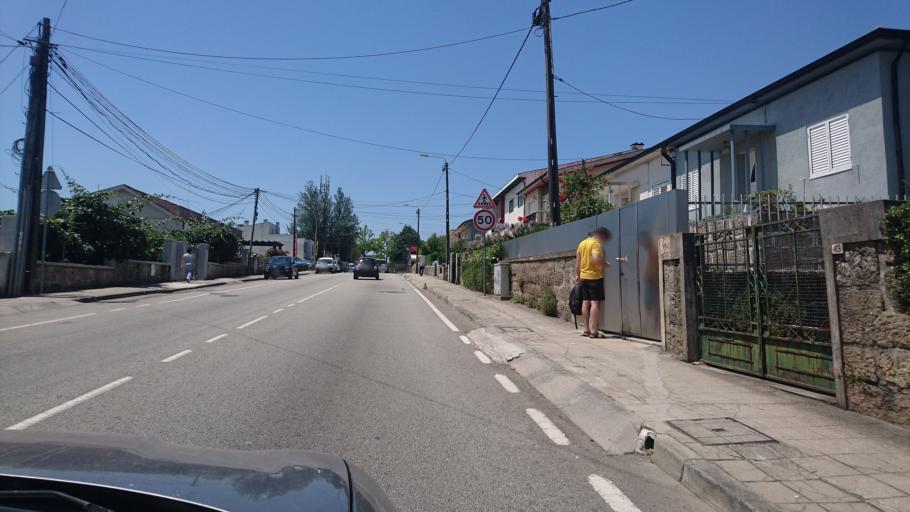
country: PT
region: Porto
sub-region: Gondomar
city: Baguim do Monte
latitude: 41.2047
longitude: -8.5522
